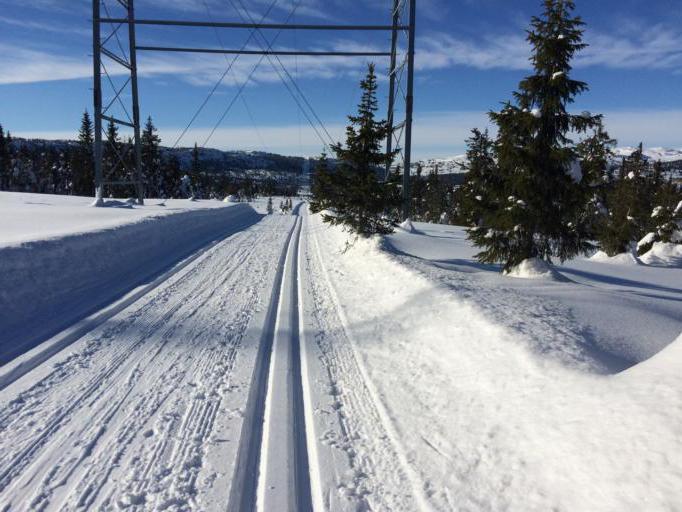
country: NO
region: Oppland
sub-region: Gausdal
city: Segalstad bru
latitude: 61.3163
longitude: 10.0989
